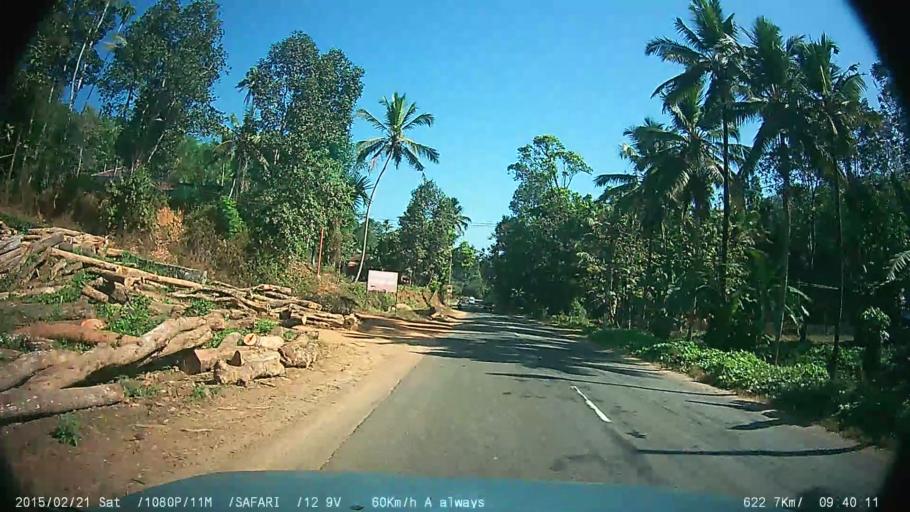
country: IN
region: Kerala
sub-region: Kottayam
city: Palackattumala
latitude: 9.7860
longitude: 76.5778
